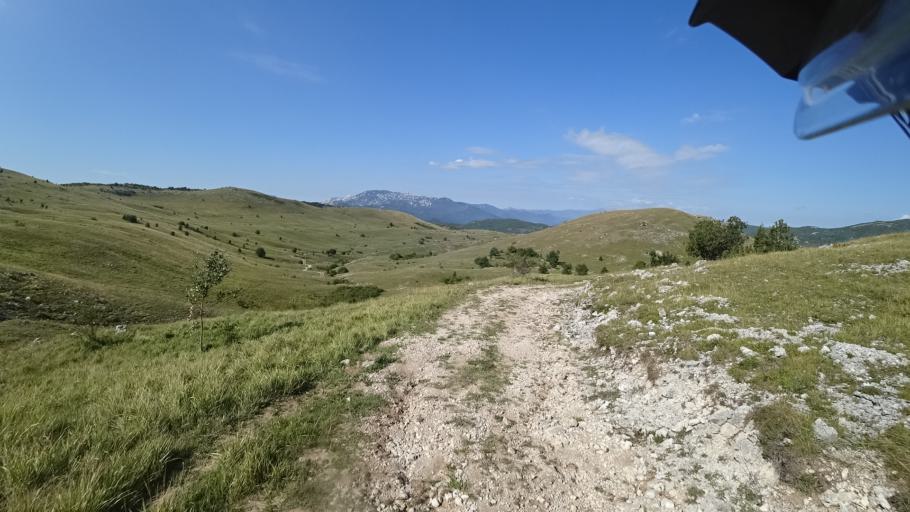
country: HR
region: Zadarska
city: Gracac
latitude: 44.3018
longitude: 15.9673
